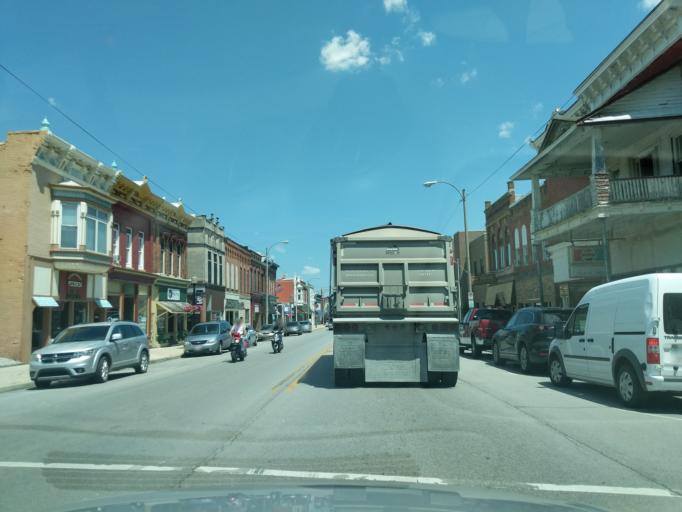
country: US
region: Indiana
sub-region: Noble County
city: Ligonier
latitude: 41.4629
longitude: -85.5876
